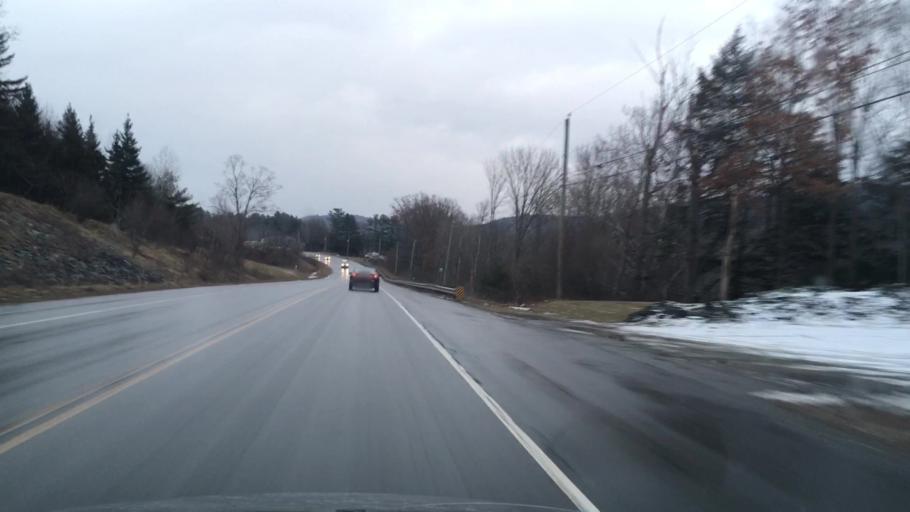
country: US
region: New Hampshire
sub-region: Sullivan County
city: Claremont
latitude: 43.3645
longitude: -72.2934
